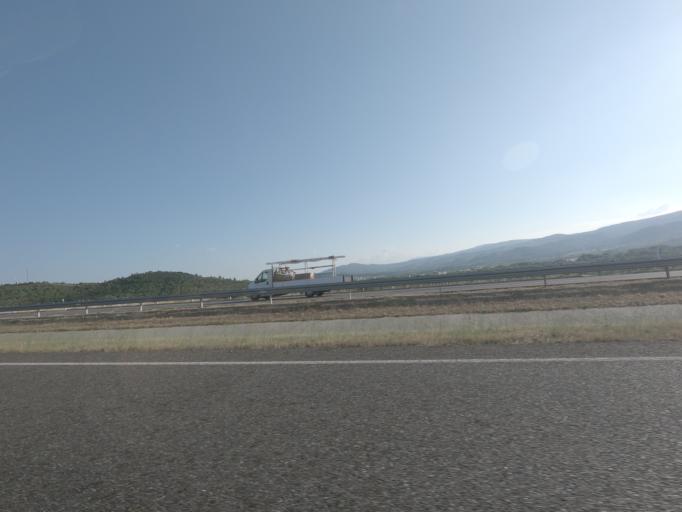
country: ES
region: Galicia
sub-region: Provincia de Ourense
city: Oimbra
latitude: 41.8644
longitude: -7.4287
